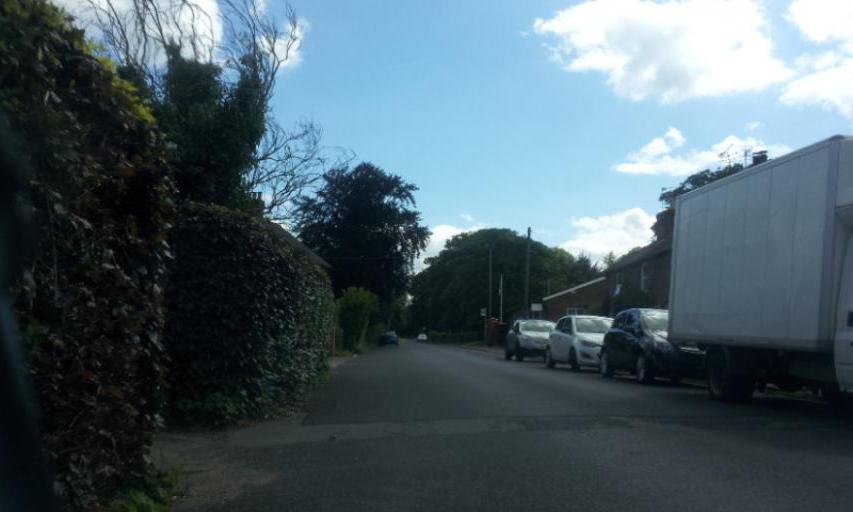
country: GB
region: England
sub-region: Kent
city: Maidstone
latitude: 51.2308
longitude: 0.5321
